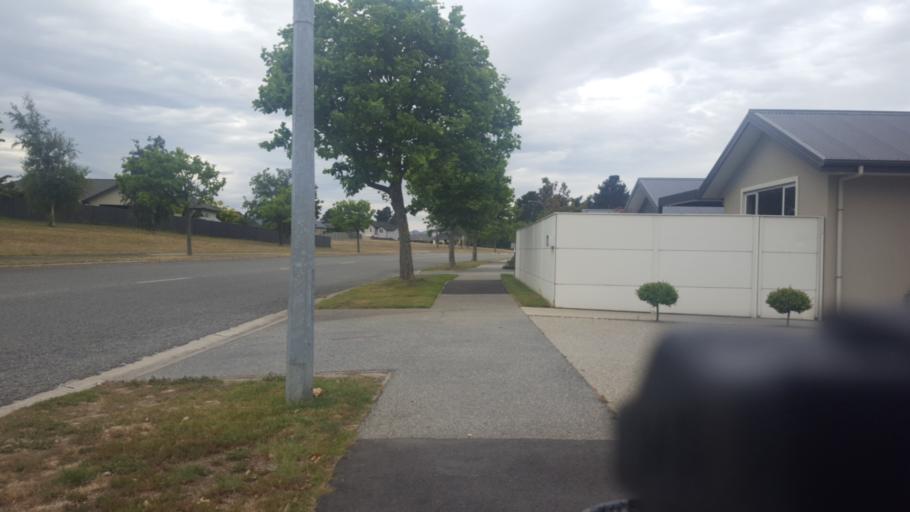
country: NZ
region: Otago
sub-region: Queenstown-Lakes District
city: Wanaka
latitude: -45.0460
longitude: 169.1879
